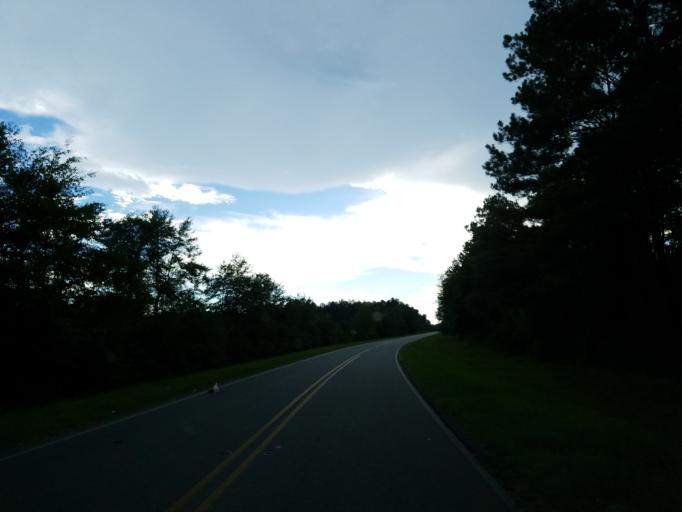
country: US
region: Georgia
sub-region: Tift County
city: Omega
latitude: 31.2551
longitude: -83.5148
